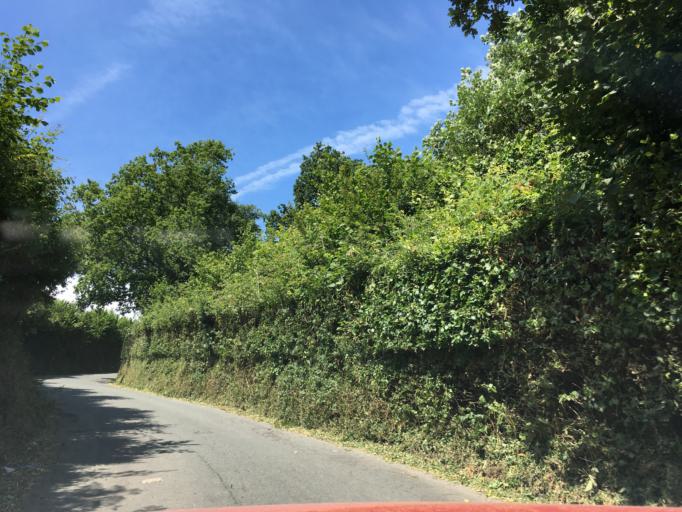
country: GB
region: Wales
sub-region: Caerphilly County Borough
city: Machen
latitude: 51.5487
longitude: -3.1410
